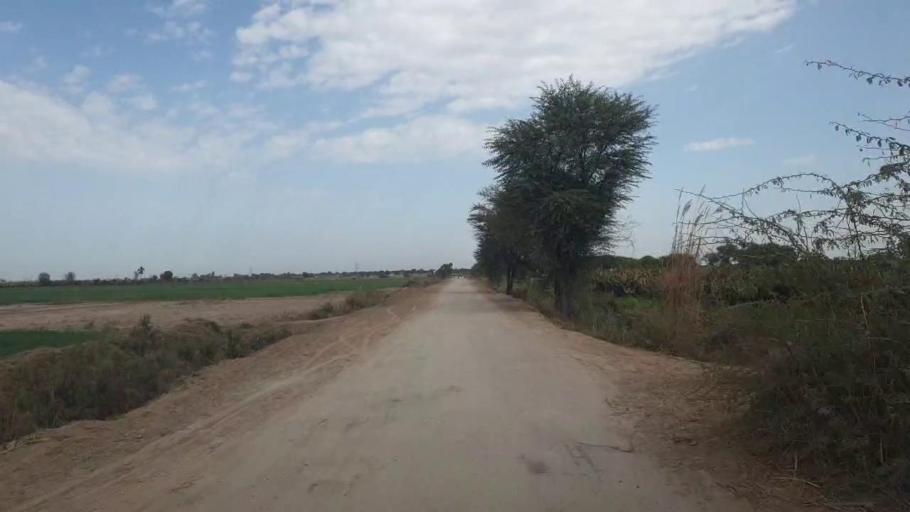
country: PK
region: Sindh
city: Sakrand
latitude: 26.0058
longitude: 68.3452
